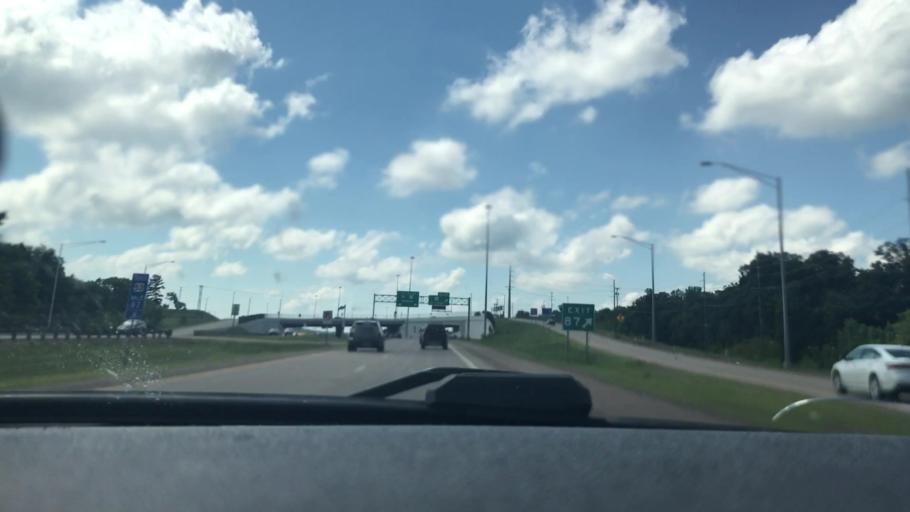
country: US
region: Wisconsin
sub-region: Eau Claire County
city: Altoona
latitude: 44.7990
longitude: -91.4562
